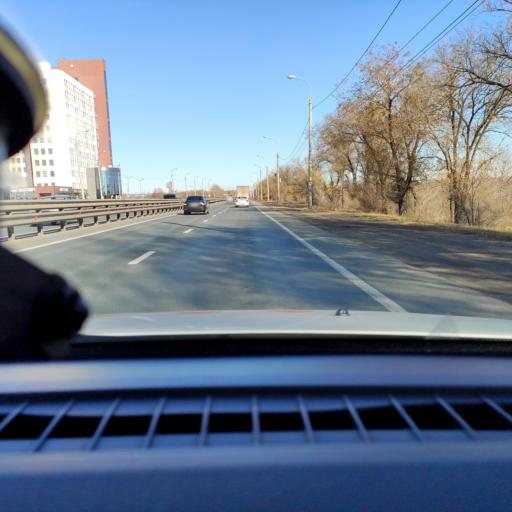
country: RU
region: Samara
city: Samara
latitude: 53.1154
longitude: 50.1666
